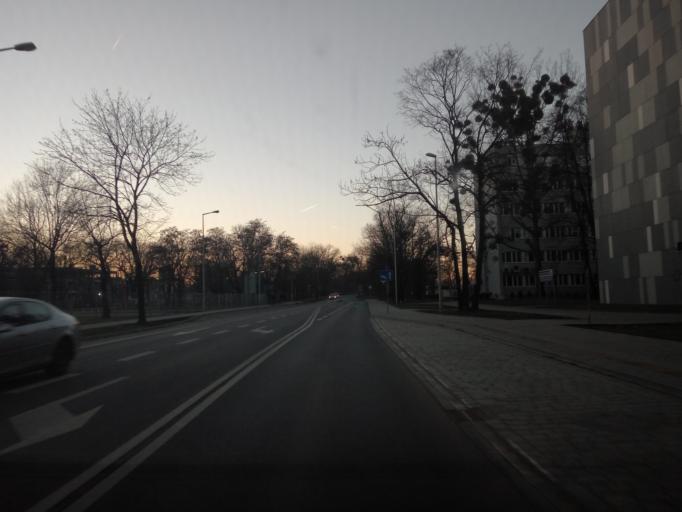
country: PL
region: Lower Silesian Voivodeship
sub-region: Powiat wroclawski
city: Wroclaw
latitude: 51.1138
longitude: 16.9930
